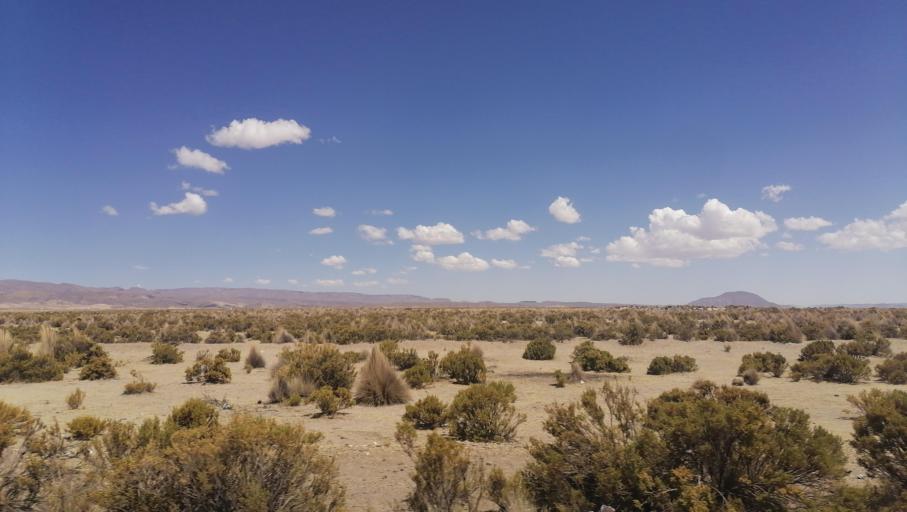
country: BO
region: Oruro
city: Challapata
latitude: -19.1709
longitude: -66.7894
